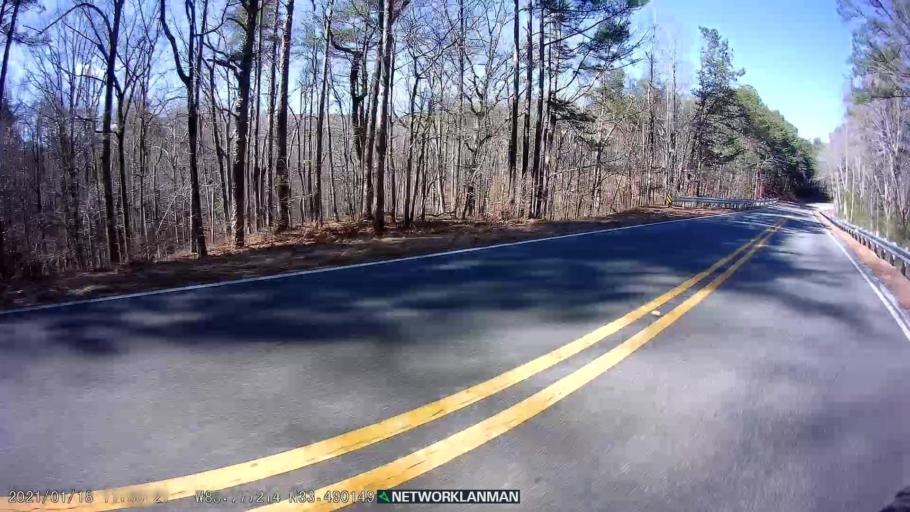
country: US
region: Alabama
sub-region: Calhoun County
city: Oxford
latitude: 33.4905
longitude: -85.7773
